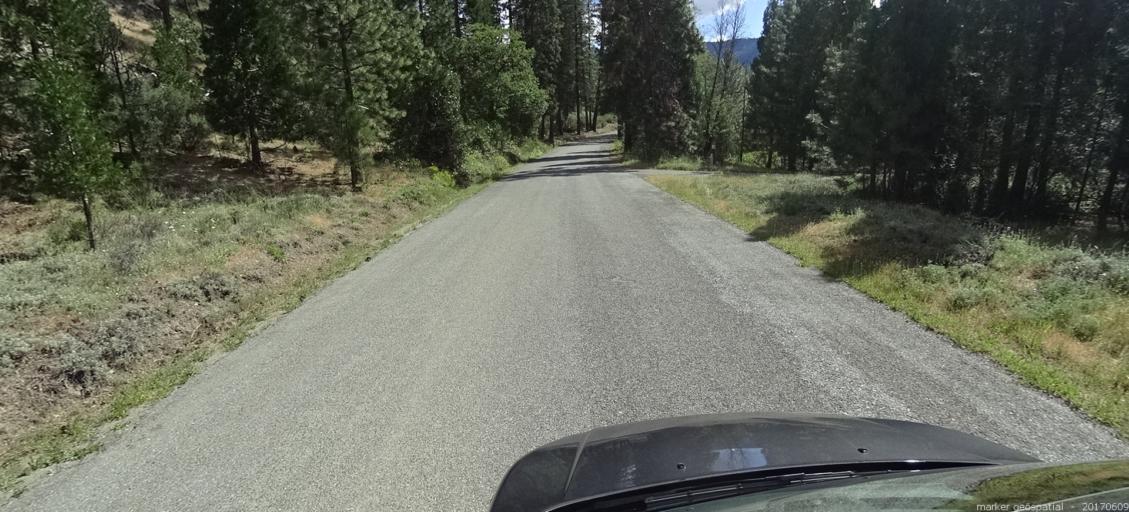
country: US
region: California
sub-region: Siskiyou County
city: Yreka
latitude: 41.3306
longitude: -122.8393
